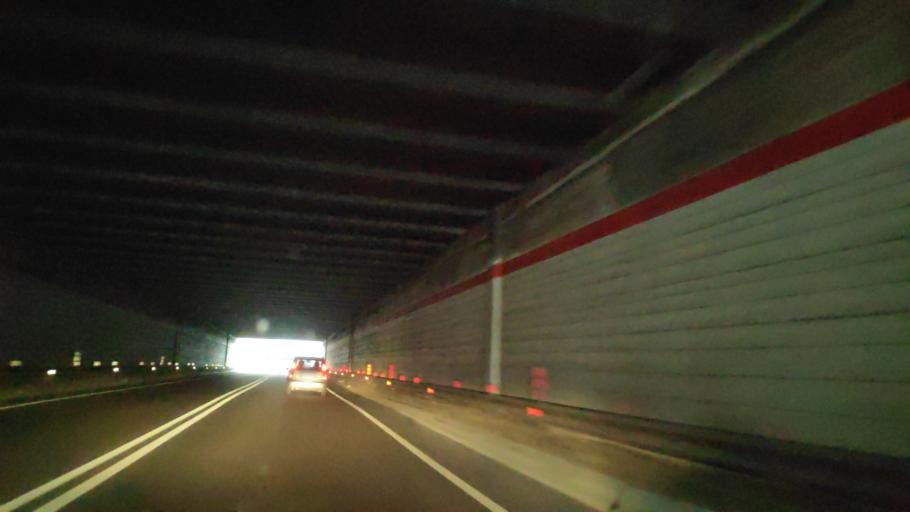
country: IT
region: Calabria
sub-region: Provincia di Catanzaro
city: Soverato Superiore
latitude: 38.6942
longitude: 16.5389
